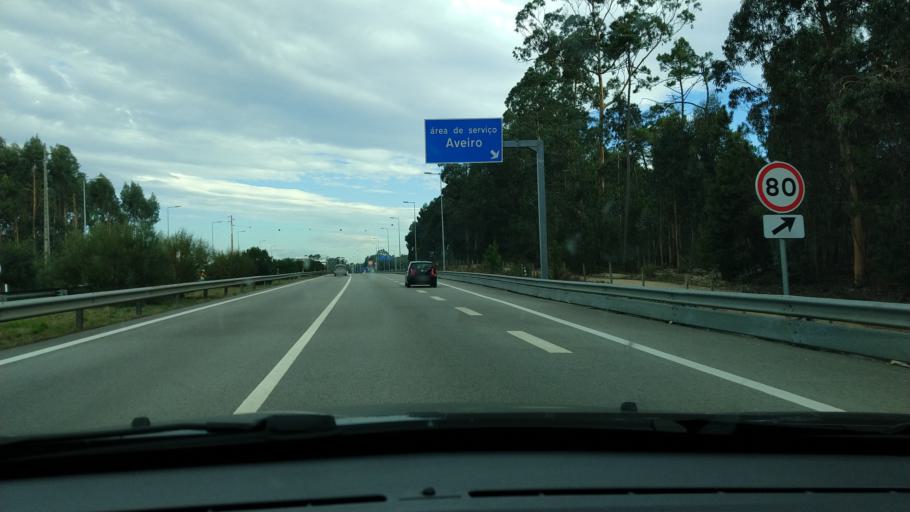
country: PT
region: Aveiro
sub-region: Aveiro
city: Eixo
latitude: 40.6569
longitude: -8.5927
